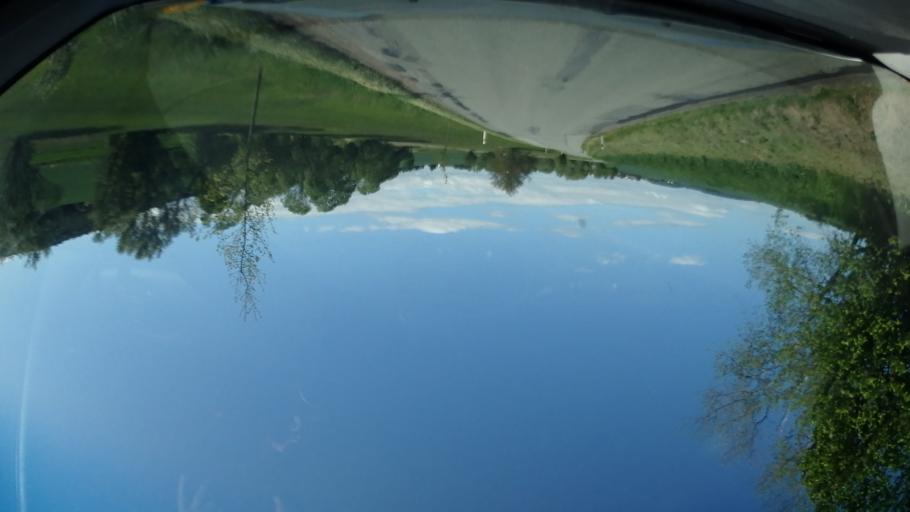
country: CZ
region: South Moravian
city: Velke Opatovice
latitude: 49.6654
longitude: 16.6335
